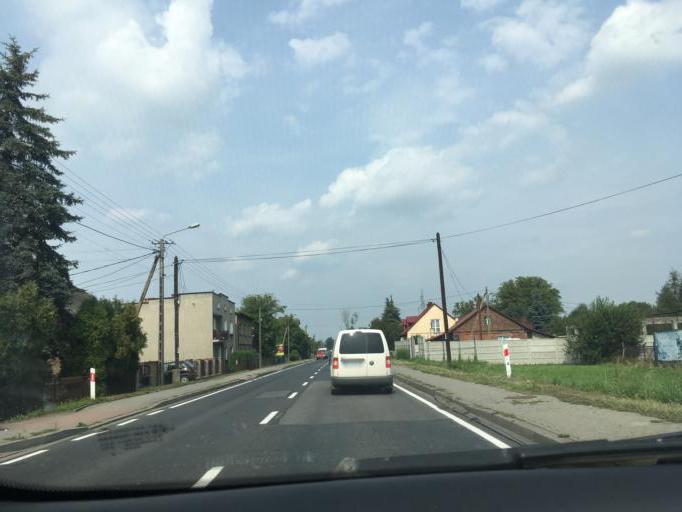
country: PL
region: Lesser Poland Voivodeship
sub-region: Powiat oswiecimski
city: Babice
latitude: 50.0525
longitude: 19.2021
